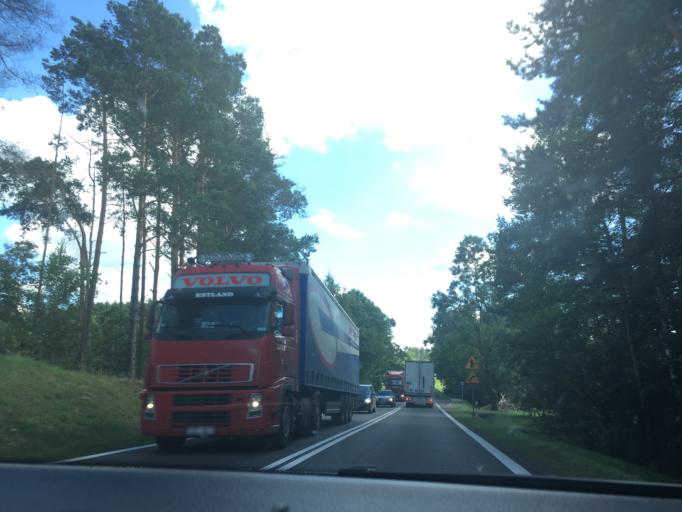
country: PL
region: Podlasie
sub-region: Powiat sokolski
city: Suchowola
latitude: 53.6612
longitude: 23.1265
